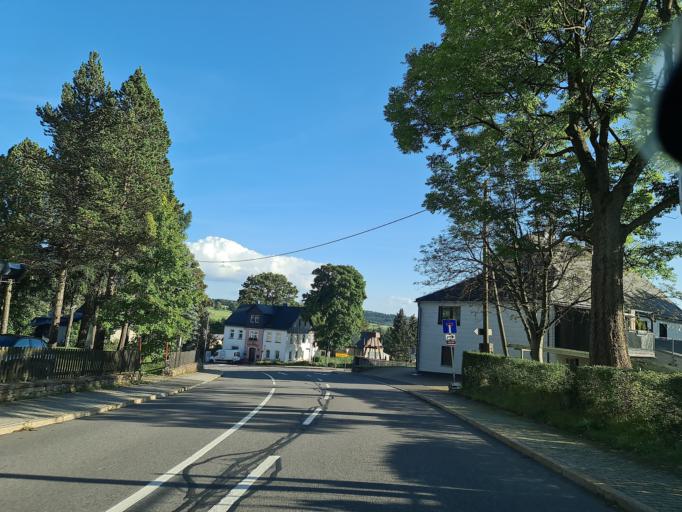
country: DE
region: Saxony
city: Deutschneudorf
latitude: 50.6319
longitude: 13.4929
